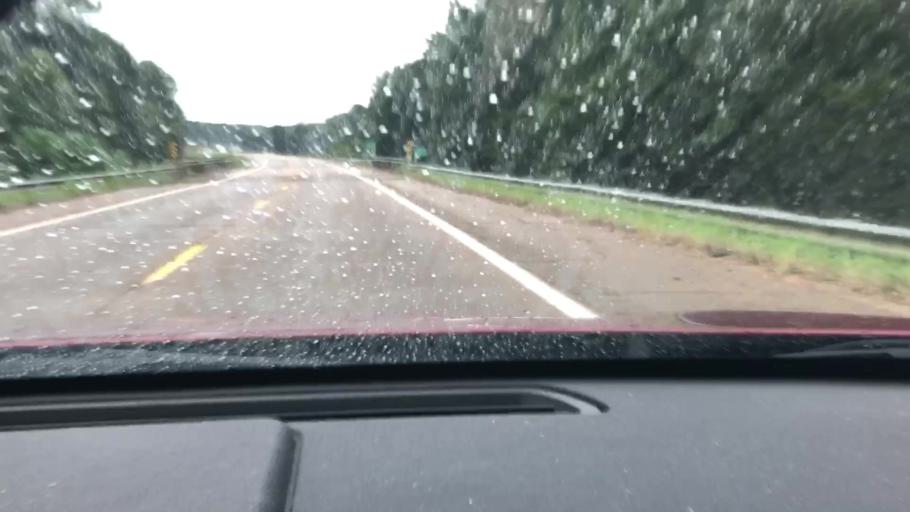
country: US
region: Arkansas
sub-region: Columbia County
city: Magnolia
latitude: 33.2970
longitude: -93.2590
